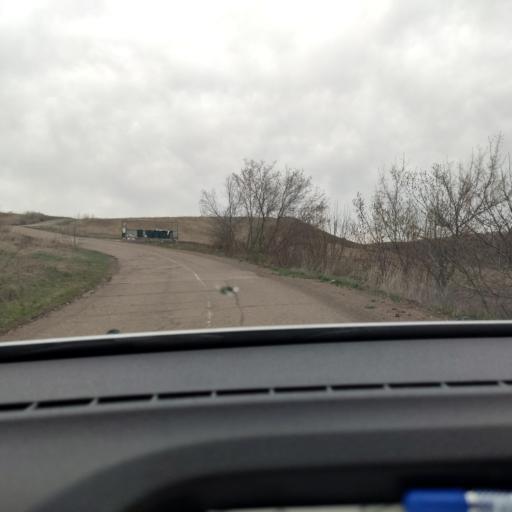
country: RU
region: Bashkortostan
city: Avdon
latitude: 54.6301
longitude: 55.5990
